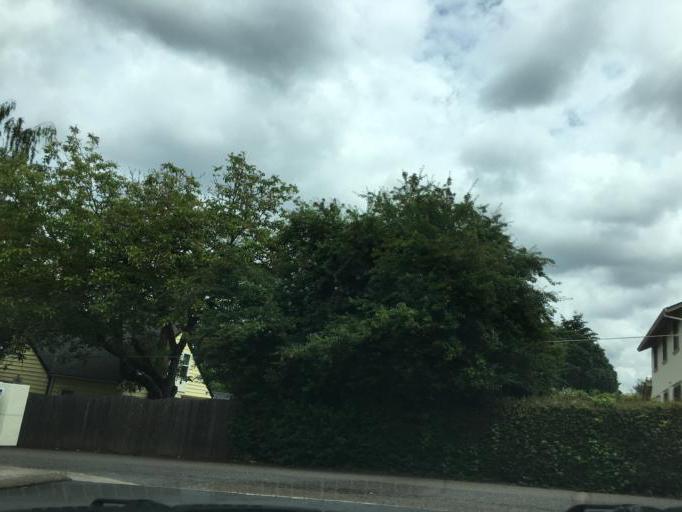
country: US
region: Oregon
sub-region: Clackamas County
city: Lake Oswego
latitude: 45.4064
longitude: -122.6764
